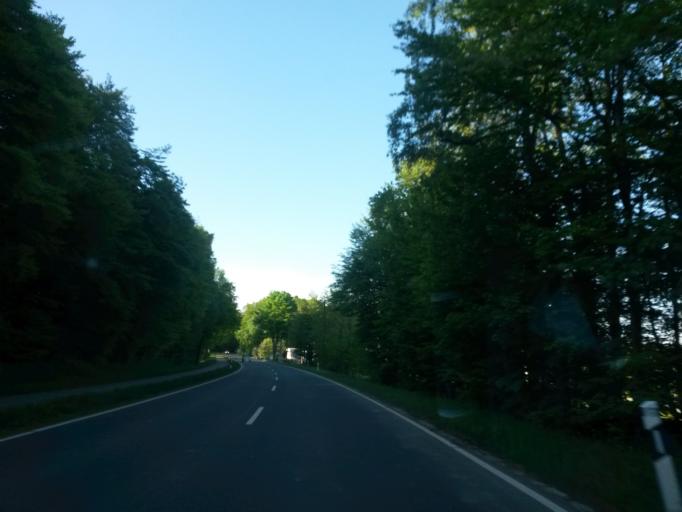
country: DE
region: North Rhine-Westphalia
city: Wiehl
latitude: 50.9263
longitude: 7.4989
